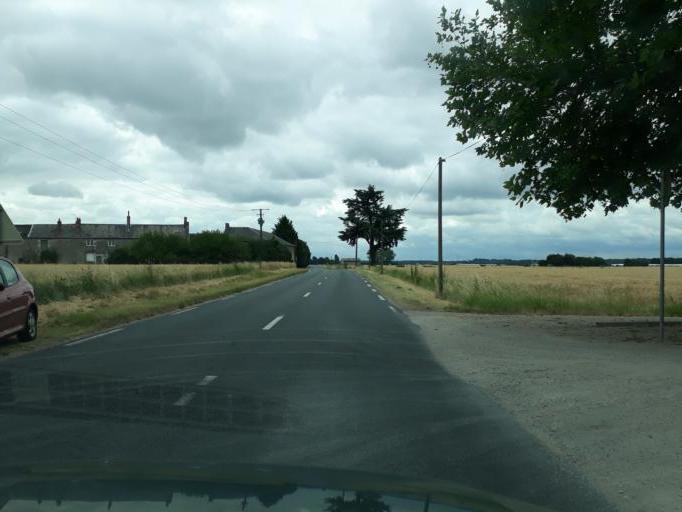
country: FR
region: Centre
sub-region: Departement du Loiret
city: Saint-Denis-en-Val
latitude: 47.8696
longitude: 1.9408
